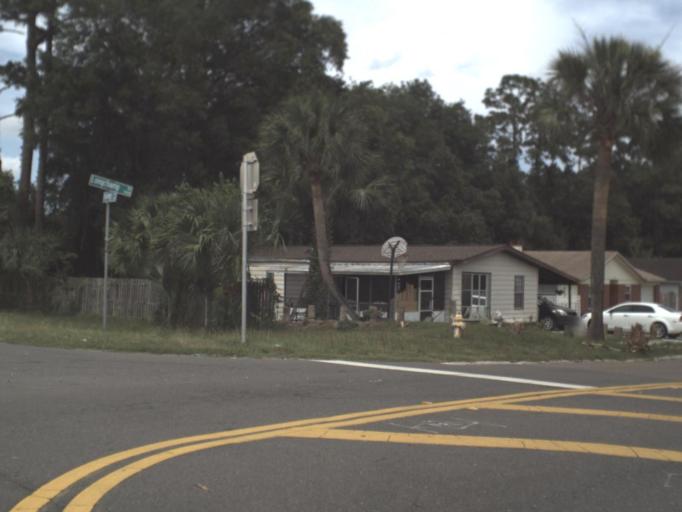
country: US
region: Florida
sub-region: Clay County
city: Bellair-Meadowbrook Terrace
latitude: 30.2108
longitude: -81.7378
